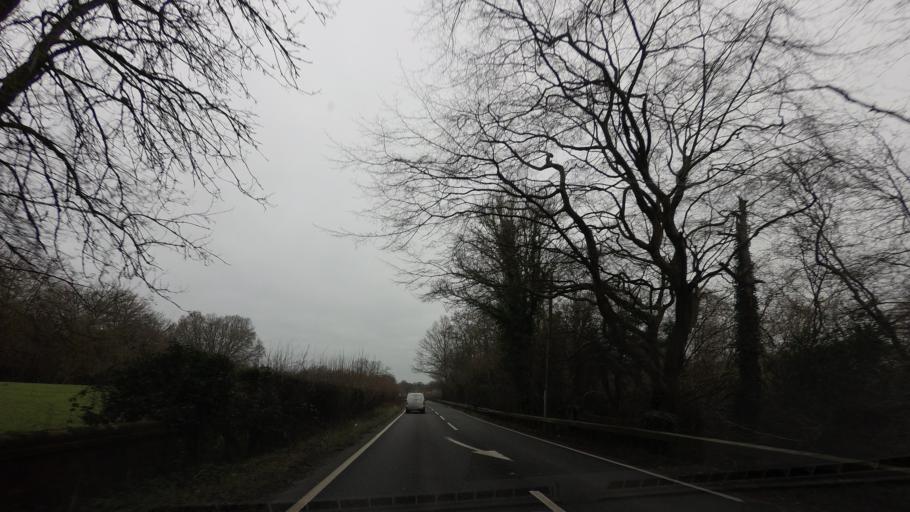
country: GB
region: England
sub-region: East Sussex
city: Saint Leonards-on-Sea
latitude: 50.9028
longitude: 0.5520
